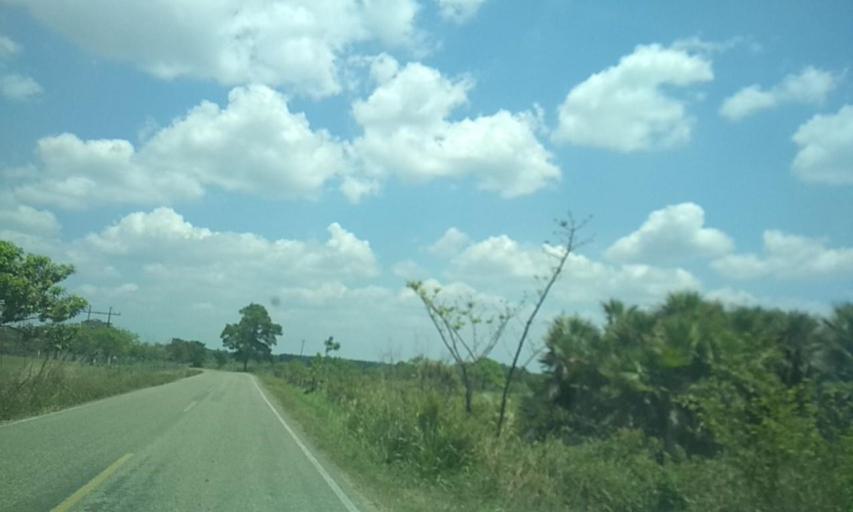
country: MX
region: Tabasco
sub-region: Huimanguillo
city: Huapacal 1ra. Seccion
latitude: 17.7569
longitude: -93.7747
